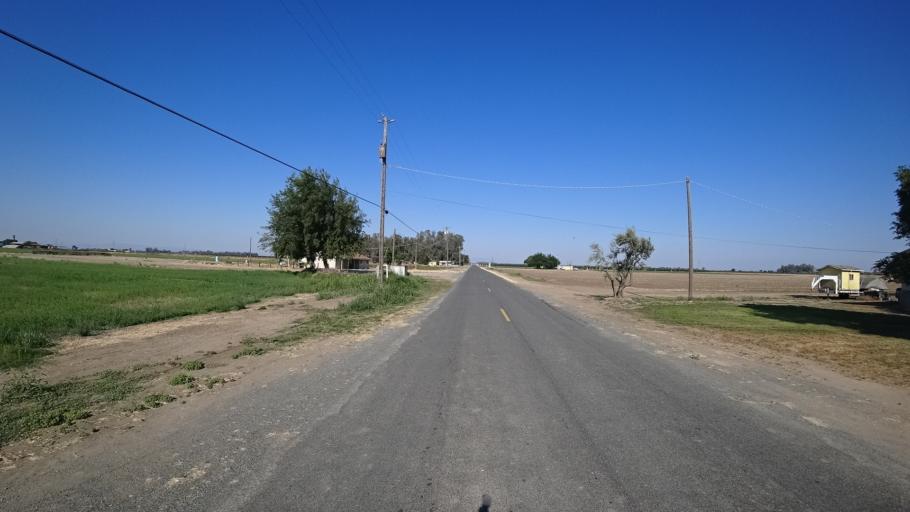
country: US
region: California
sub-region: Fresno County
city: Riverdale
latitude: 36.3657
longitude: -119.8756
